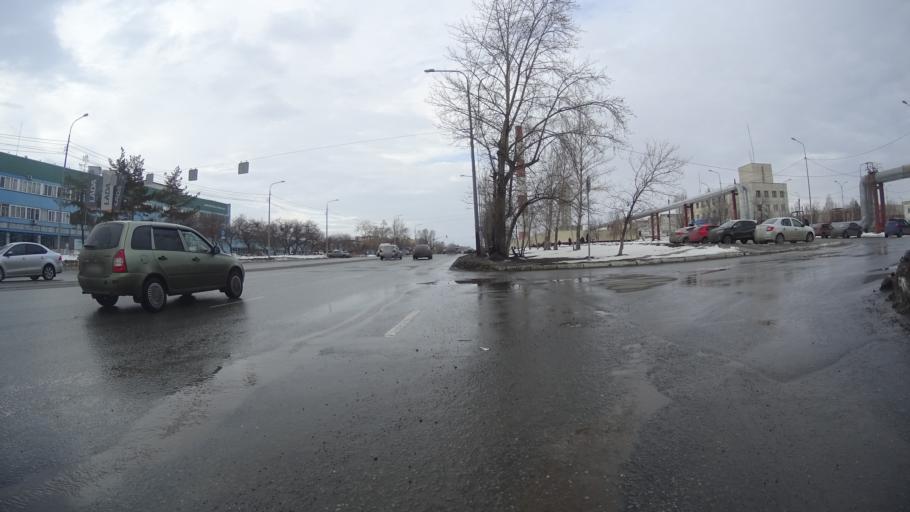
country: RU
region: Chelyabinsk
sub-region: Gorod Chelyabinsk
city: Chelyabinsk
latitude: 55.2041
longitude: 61.3239
